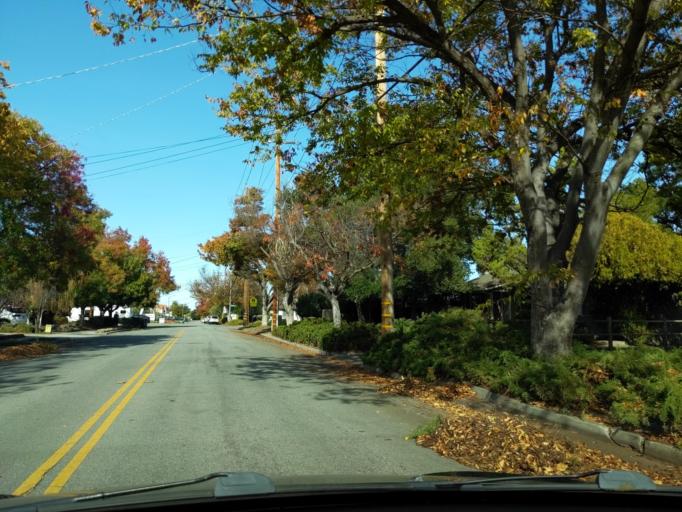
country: US
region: California
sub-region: Santa Clara County
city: Cambrian Park
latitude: 37.2462
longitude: -121.9052
